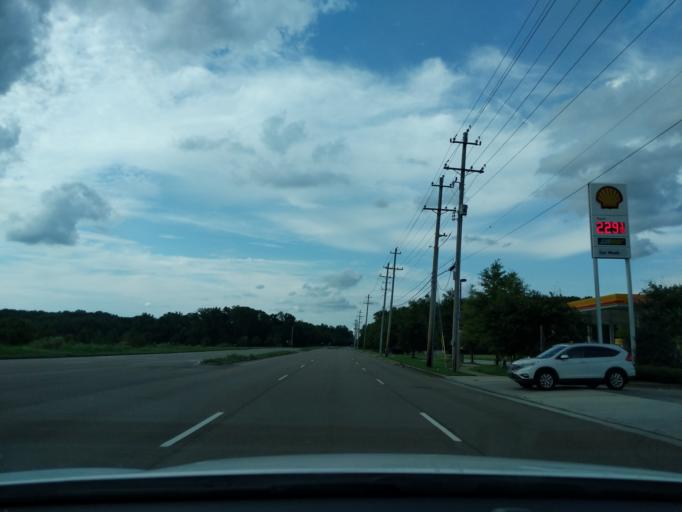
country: US
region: Tennessee
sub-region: Shelby County
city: Germantown
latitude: 35.0288
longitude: -89.7596
